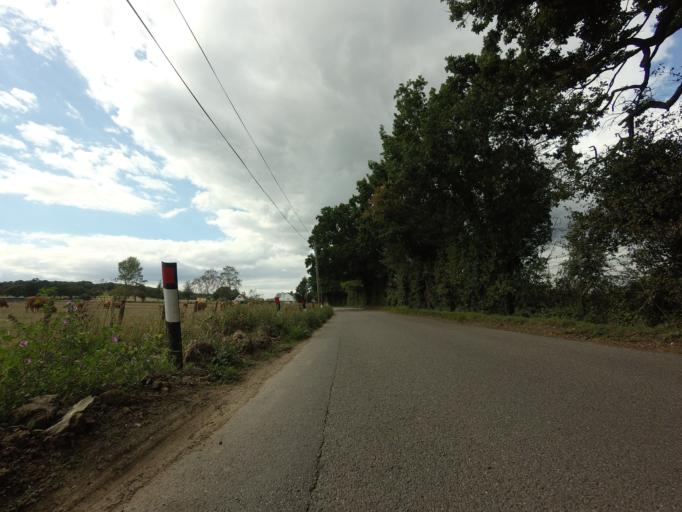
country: GB
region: England
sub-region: Kent
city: Marden
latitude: 51.1594
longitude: 0.4357
